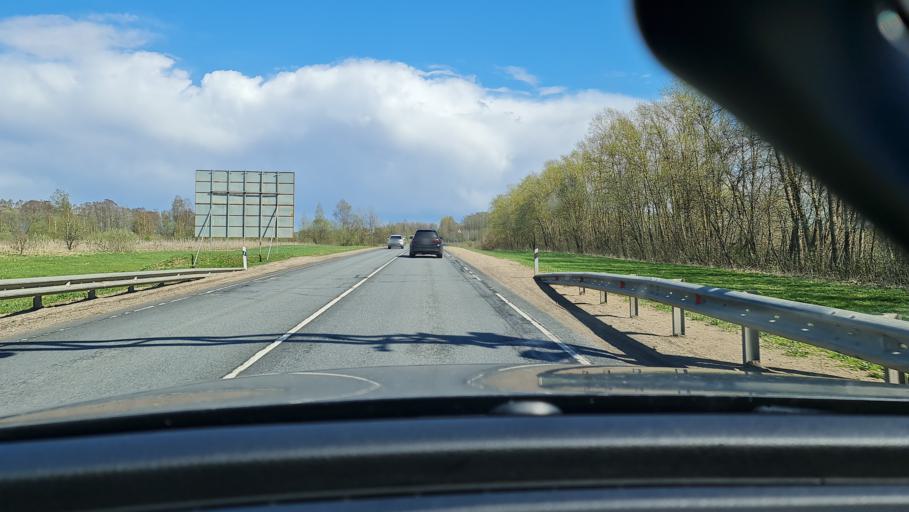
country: RU
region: Tverskaya
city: Rzhev
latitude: 56.2194
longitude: 34.3567
